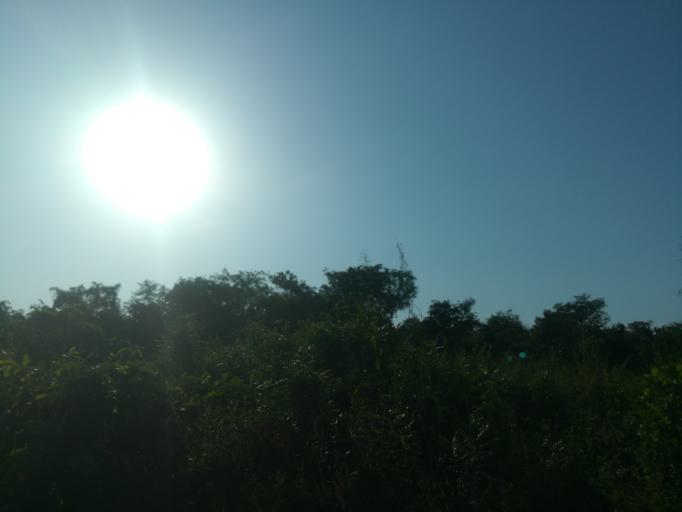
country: NG
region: Ogun
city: Abeokuta
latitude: 7.2499
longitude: 3.3004
